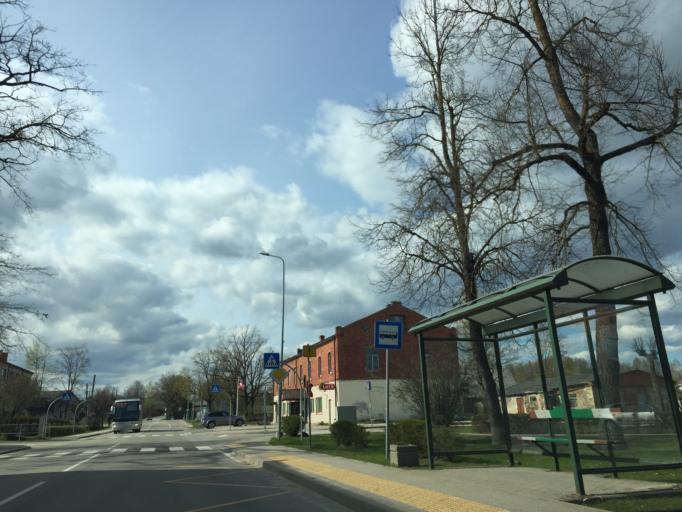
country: LV
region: Plavinu
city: Plavinas
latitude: 56.6166
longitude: 25.7211
